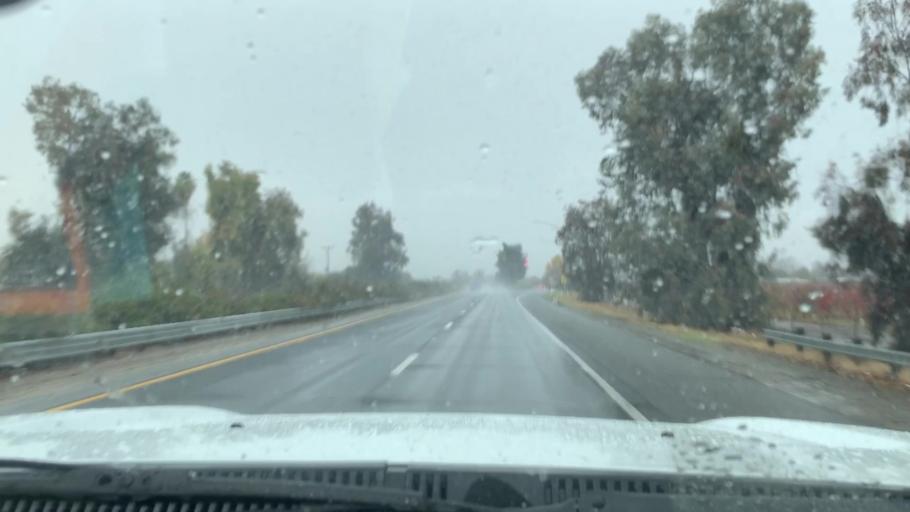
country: US
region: California
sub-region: Tulare County
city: Earlimart
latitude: 35.8731
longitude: -119.2705
